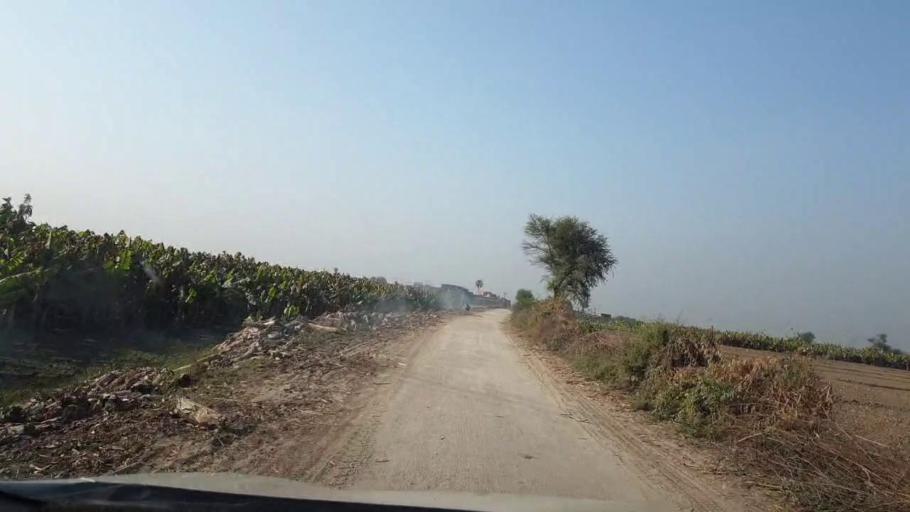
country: PK
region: Sindh
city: Bhit Shah
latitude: 25.6868
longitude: 68.5409
